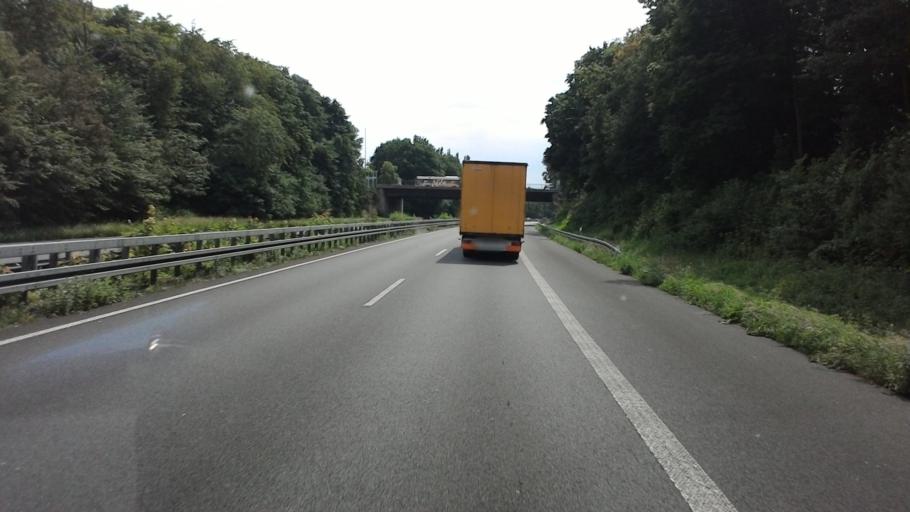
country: DE
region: North Rhine-Westphalia
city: Stolberg
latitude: 50.7795
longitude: 6.1774
